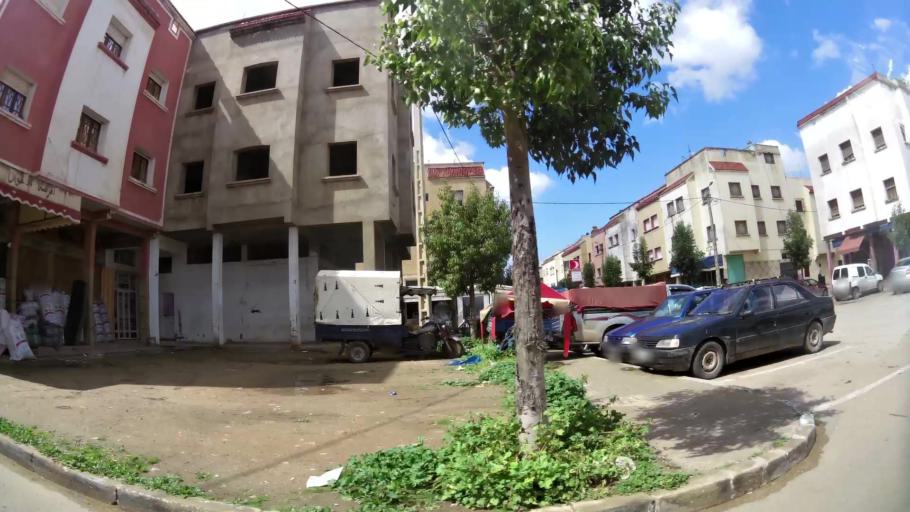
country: MA
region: Grand Casablanca
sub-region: Mediouna
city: Mediouna
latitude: 33.3666
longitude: -7.5290
